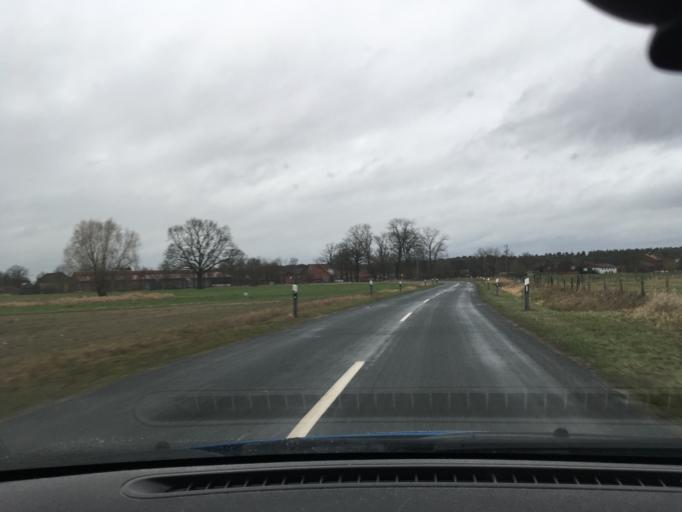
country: DE
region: Schleswig-Holstein
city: Lanze
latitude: 53.3650
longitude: 10.6361
